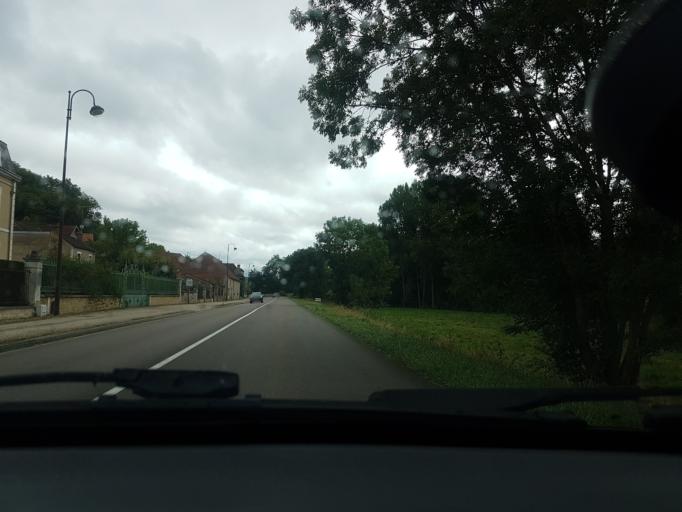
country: FR
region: Bourgogne
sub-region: Departement de l'Yonne
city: Joux-la-Ville
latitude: 47.5809
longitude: 3.7789
